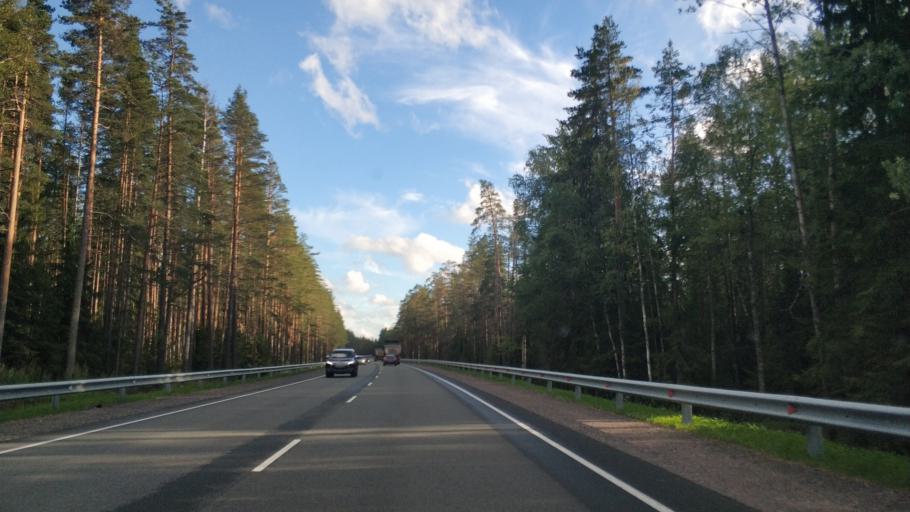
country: RU
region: Leningrad
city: Priozersk
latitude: 60.8915
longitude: 30.1597
